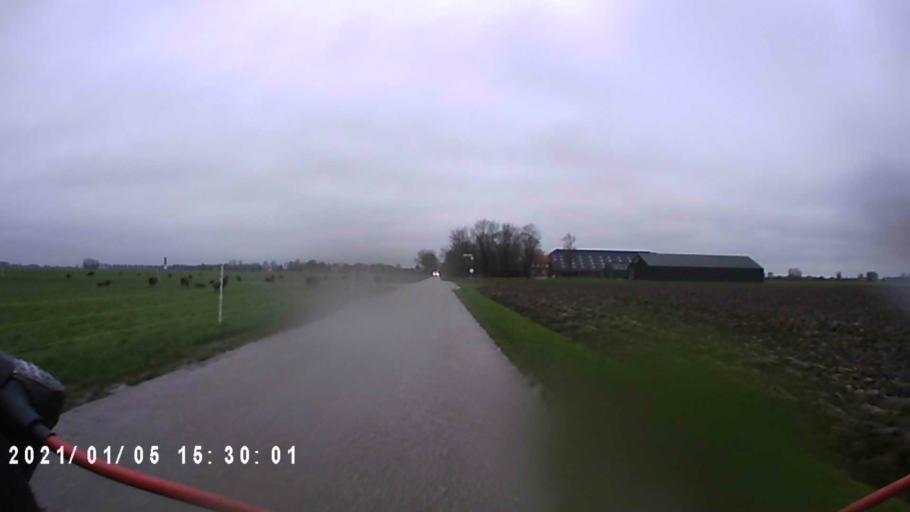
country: DE
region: Lower Saxony
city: Bunde
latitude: 53.2106
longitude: 7.1908
